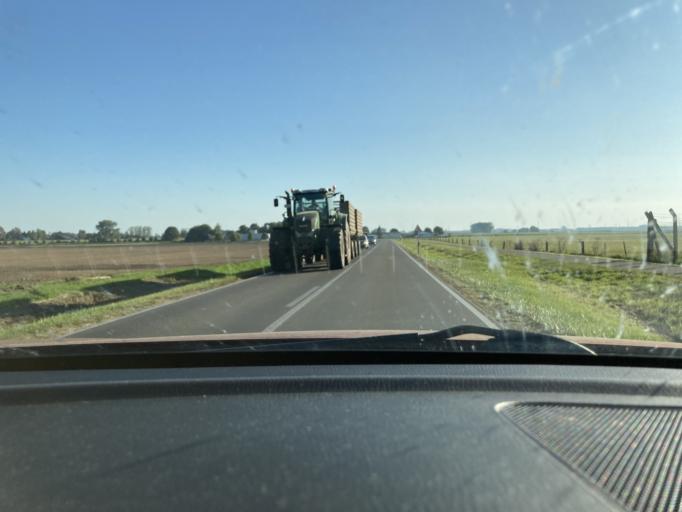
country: DE
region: Mecklenburg-Vorpommern
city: Anklam
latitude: 53.8330
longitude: 13.6798
